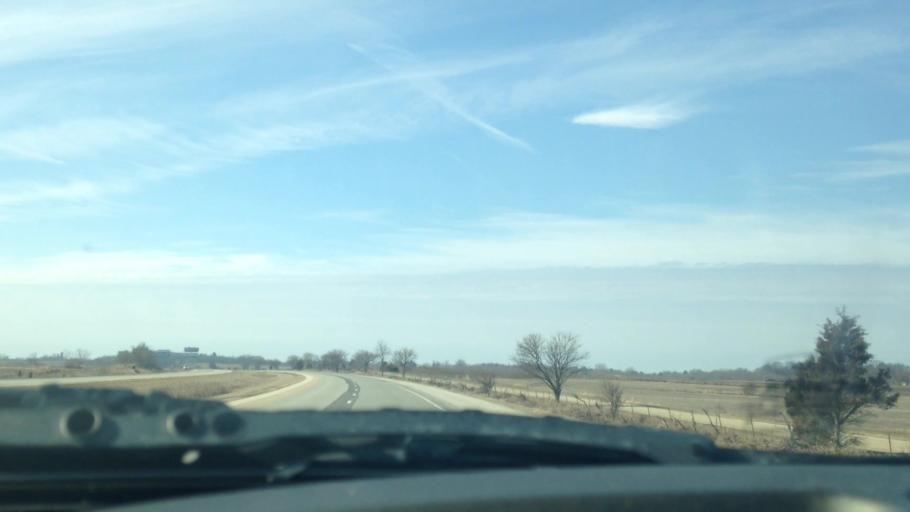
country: US
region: Illinois
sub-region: Ford County
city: Paxton
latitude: 40.5249
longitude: -88.0834
